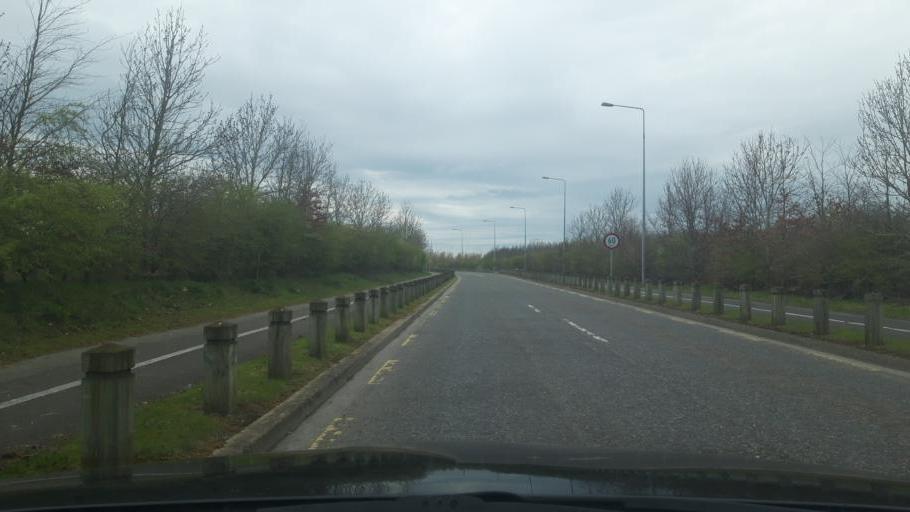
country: IE
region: Leinster
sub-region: Kildare
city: Celbridge
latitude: 53.3581
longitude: -6.5236
